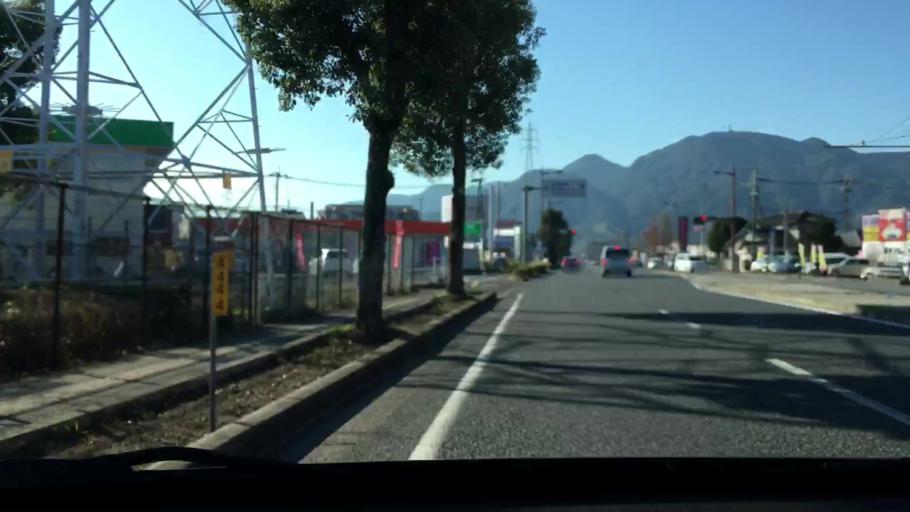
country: JP
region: Kagoshima
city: Kajiki
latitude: 31.7234
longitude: 130.6228
